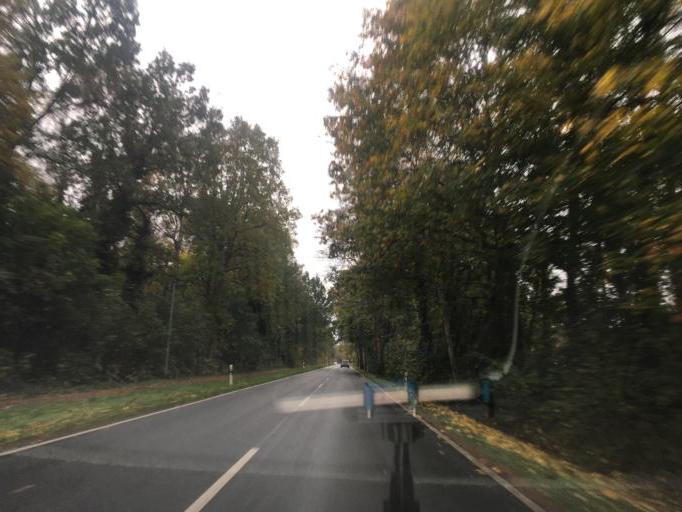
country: DE
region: Lower Saxony
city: Winsen
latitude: 52.6402
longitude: 9.9322
